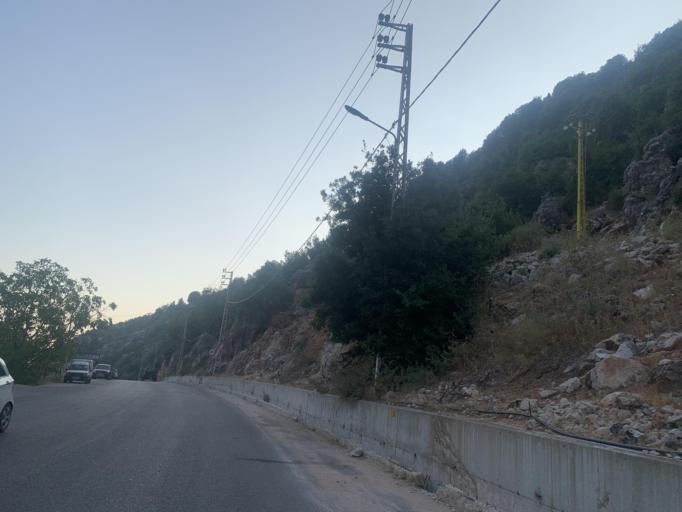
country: LB
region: Liban-Nord
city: Amioun
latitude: 34.1327
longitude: 35.8153
